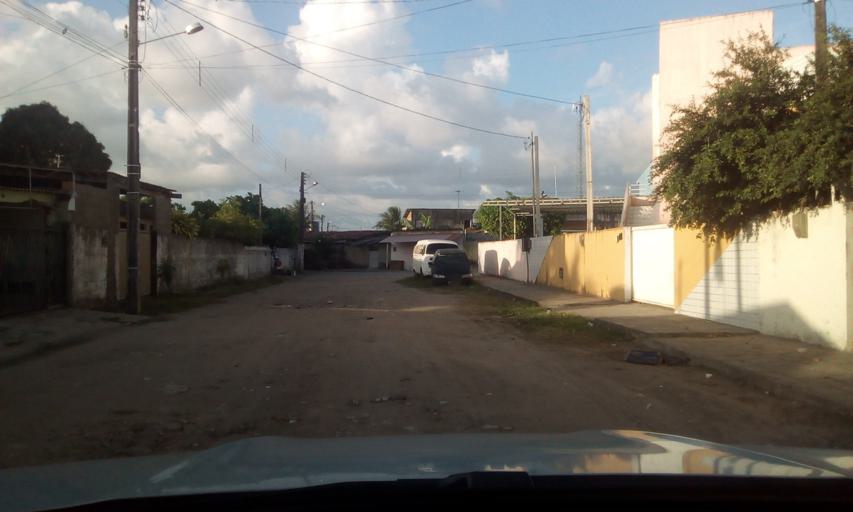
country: BR
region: Paraiba
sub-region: Conde
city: Conde
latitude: -7.2012
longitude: -34.8604
